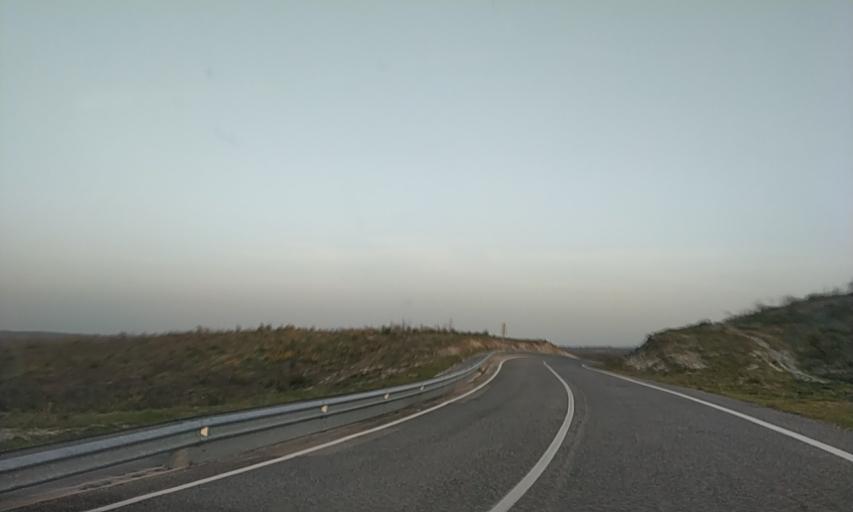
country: PT
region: Leiria
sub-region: Marinha Grande
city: Marinha Grande
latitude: 39.7451
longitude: -8.9857
